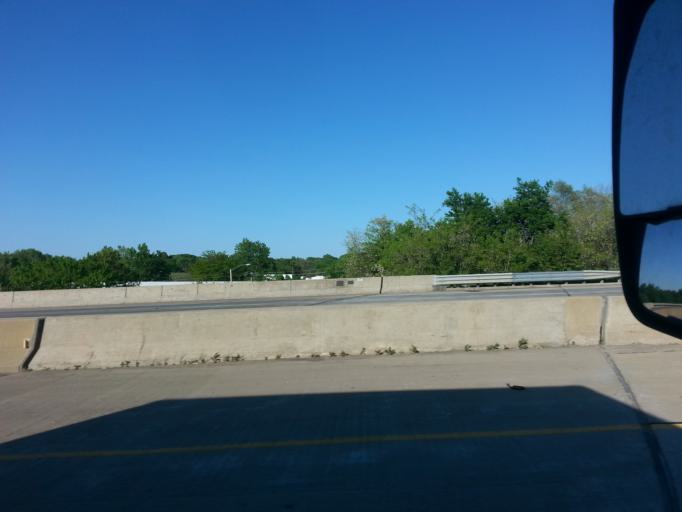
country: US
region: Illinois
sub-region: McLean County
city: Bloomington
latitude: 40.4587
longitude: -89.0274
